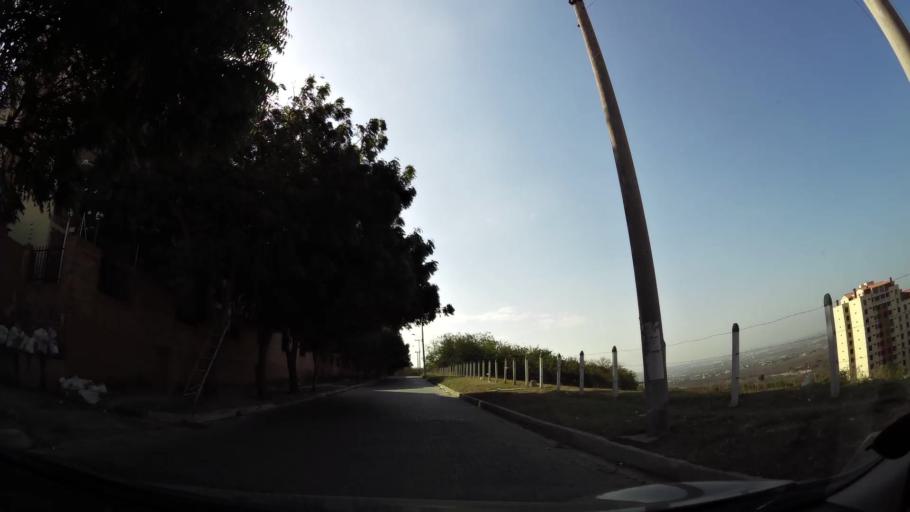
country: CO
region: Atlantico
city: Barranquilla
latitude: 11.0015
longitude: -74.8342
